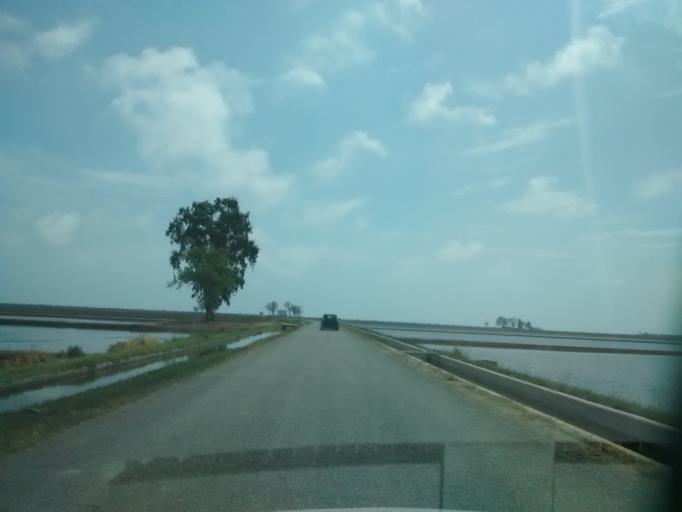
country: ES
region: Catalonia
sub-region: Provincia de Tarragona
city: Deltebre
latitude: 40.6816
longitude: 0.7960
